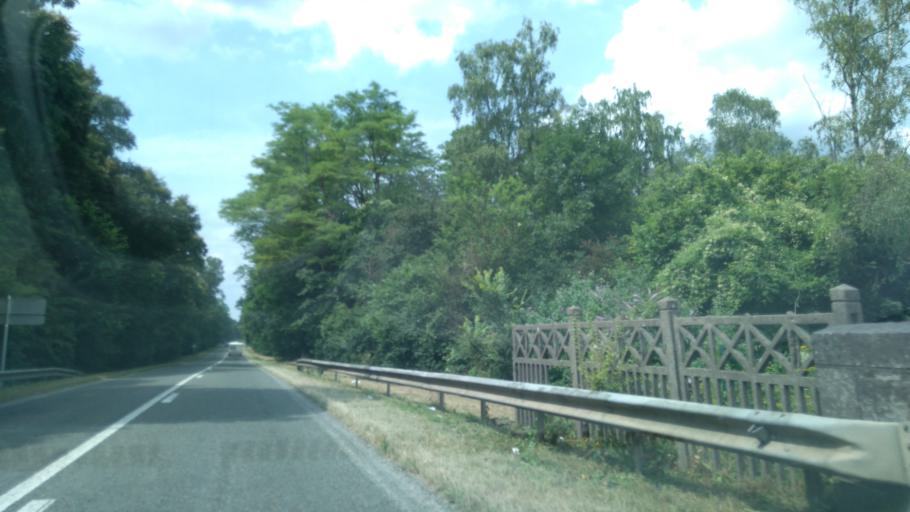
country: FR
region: Picardie
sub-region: Departement de l'Oise
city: Saint-Maximin
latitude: 49.2076
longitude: 2.4564
